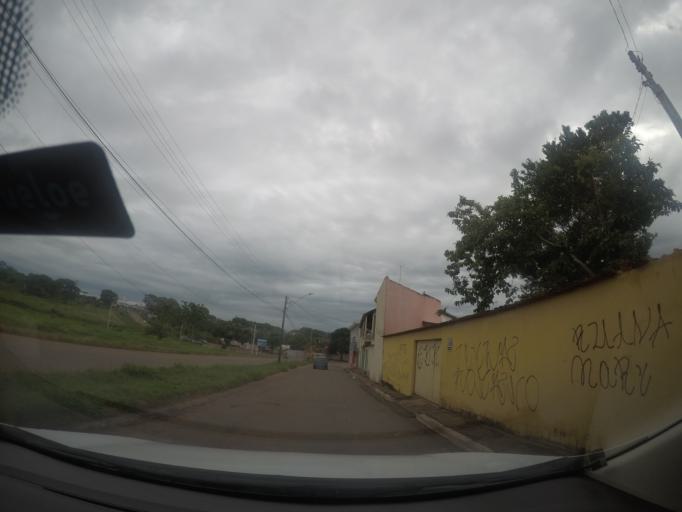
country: BR
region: Goias
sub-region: Goiania
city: Goiania
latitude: -16.6401
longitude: -49.3305
